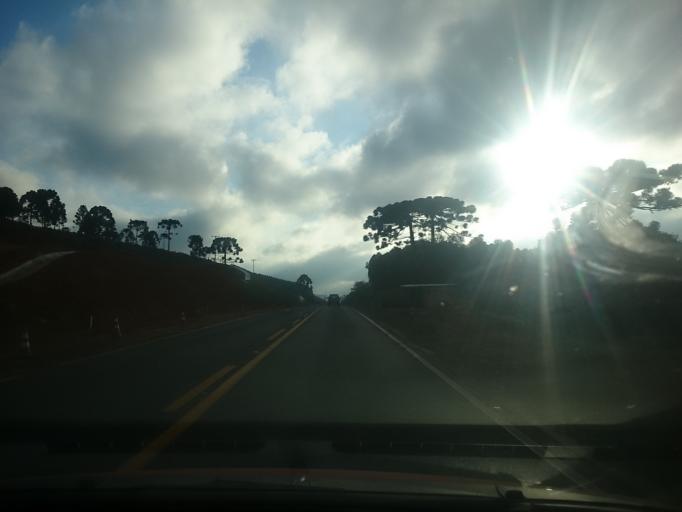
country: BR
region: Santa Catarina
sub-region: Lages
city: Lages
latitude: -28.0011
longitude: -50.5353
